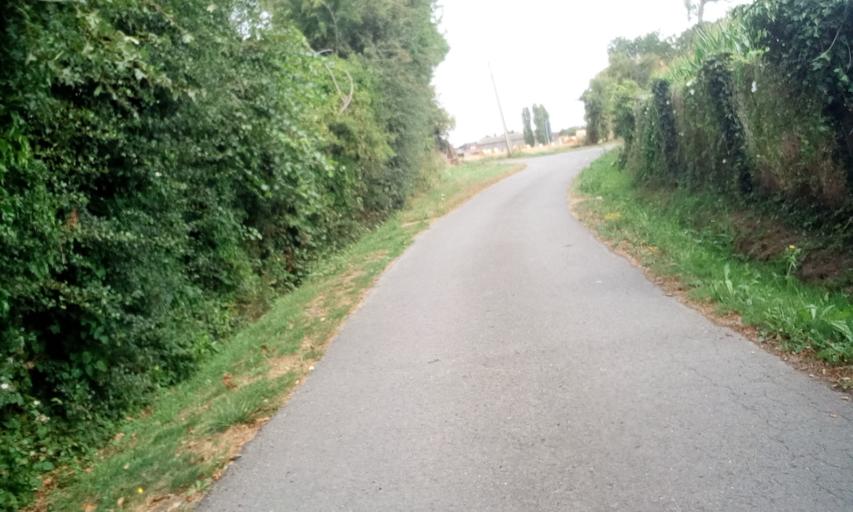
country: FR
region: Lower Normandy
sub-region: Departement du Calvados
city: Merville-Franceville-Plage
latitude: 49.2553
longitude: -0.1983
